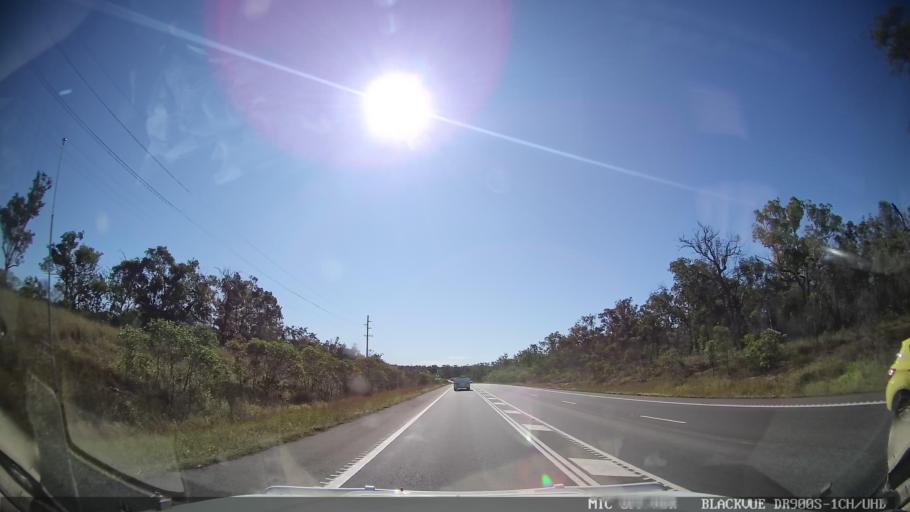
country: AU
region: Queensland
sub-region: Bundaberg
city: Childers
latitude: -25.2708
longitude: 152.3780
